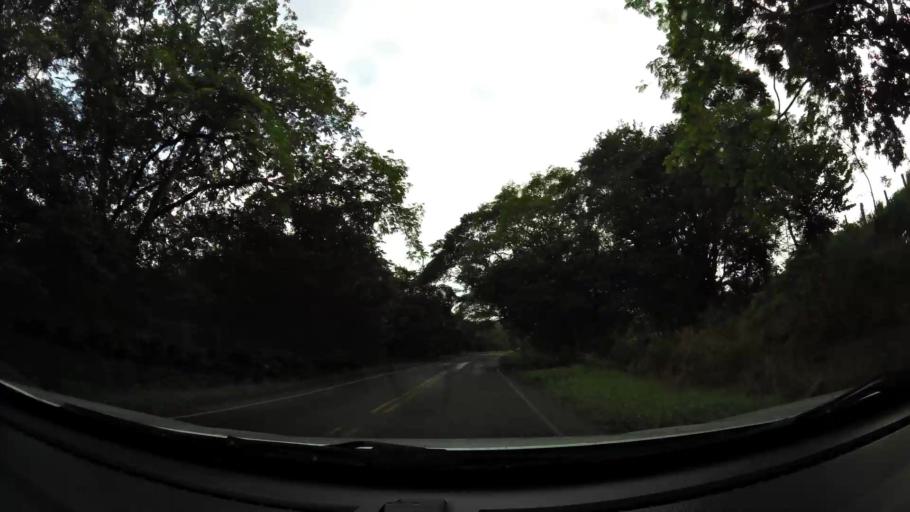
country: CR
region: Guanacaste
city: Juntas
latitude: 10.2351
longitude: -84.9833
